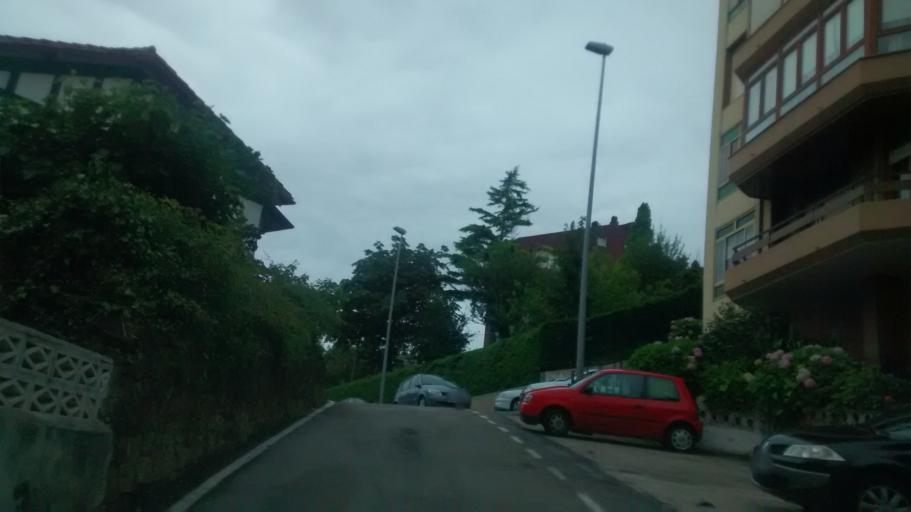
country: ES
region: Cantabria
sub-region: Provincia de Cantabria
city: Santander
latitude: 43.4654
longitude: -3.7876
